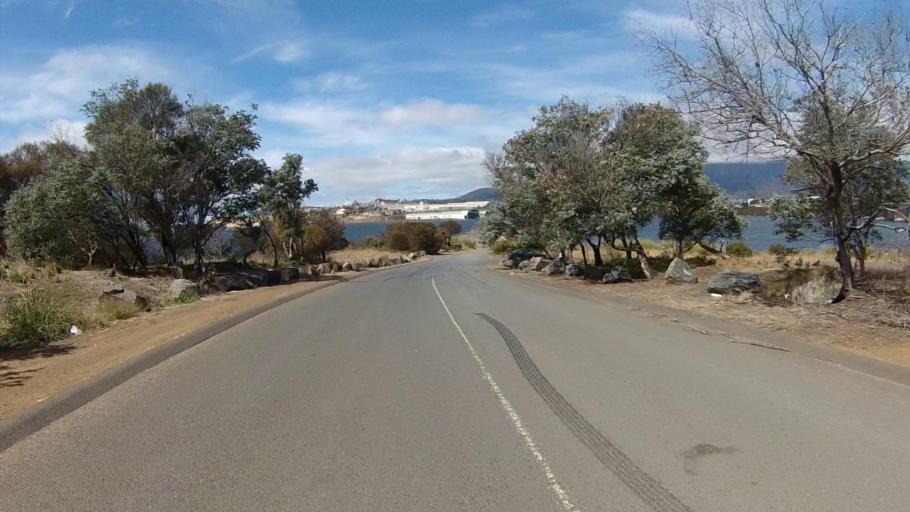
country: AU
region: Tasmania
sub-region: Glenorchy
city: Lutana
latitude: -42.8151
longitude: 147.3128
